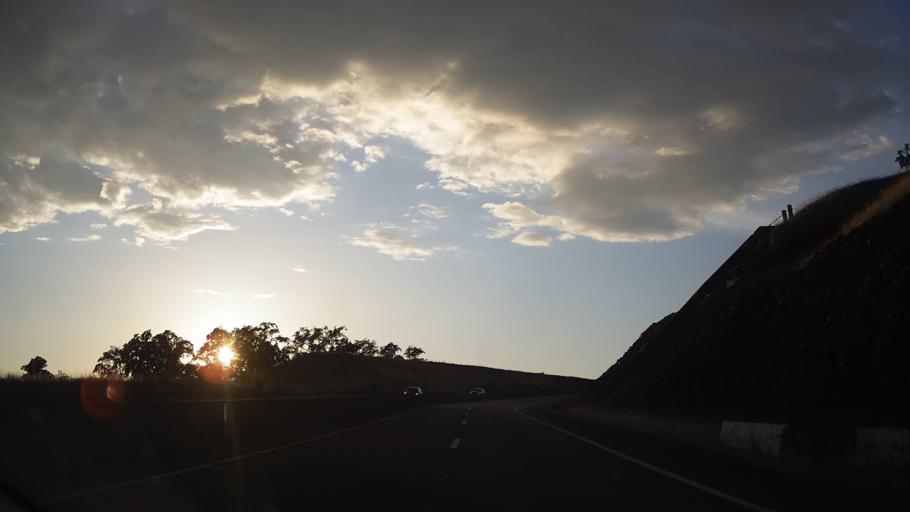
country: US
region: California
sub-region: Mendocino County
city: Redwood Valley
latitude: 39.3157
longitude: -123.2999
